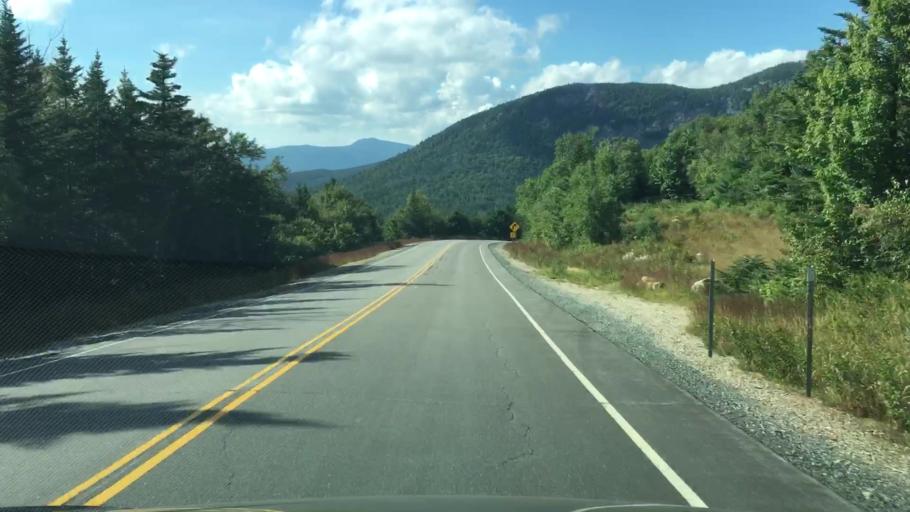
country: US
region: New Hampshire
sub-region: Grafton County
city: Woodstock
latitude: 44.0286
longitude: -71.4967
